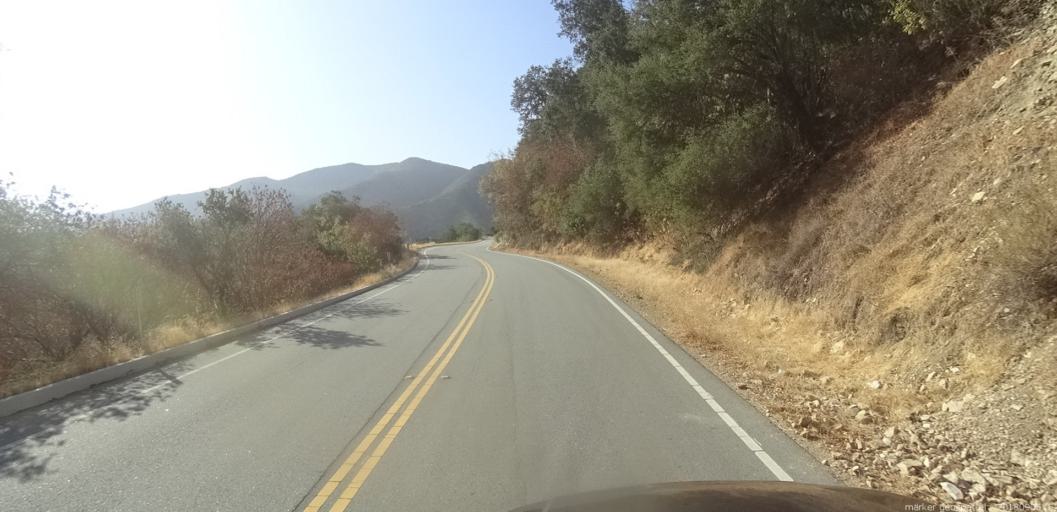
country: US
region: California
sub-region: Monterey County
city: Greenfield
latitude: 36.2530
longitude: -121.4317
